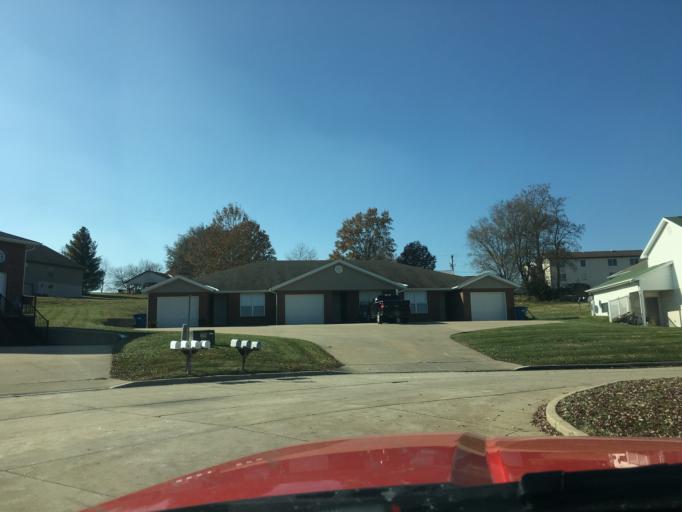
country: US
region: Missouri
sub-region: Cole County
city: Wardsville
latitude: 38.4876
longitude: -92.1738
